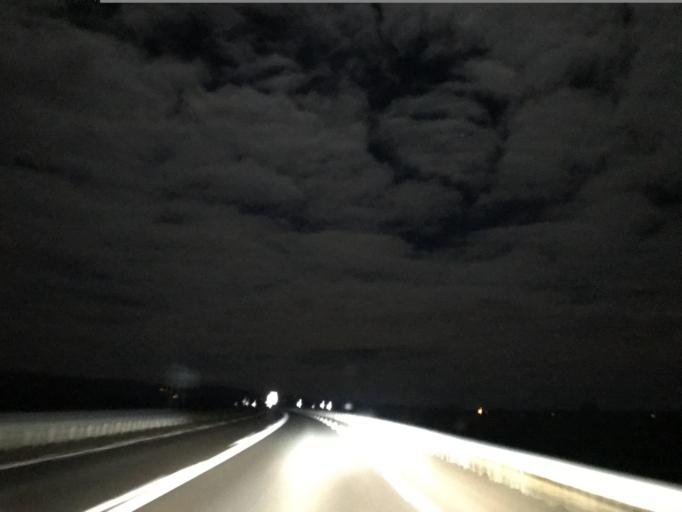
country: FR
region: Auvergne
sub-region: Departement de l'Allier
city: Saint-Yorre
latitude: 46.0581
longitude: 3.4477
